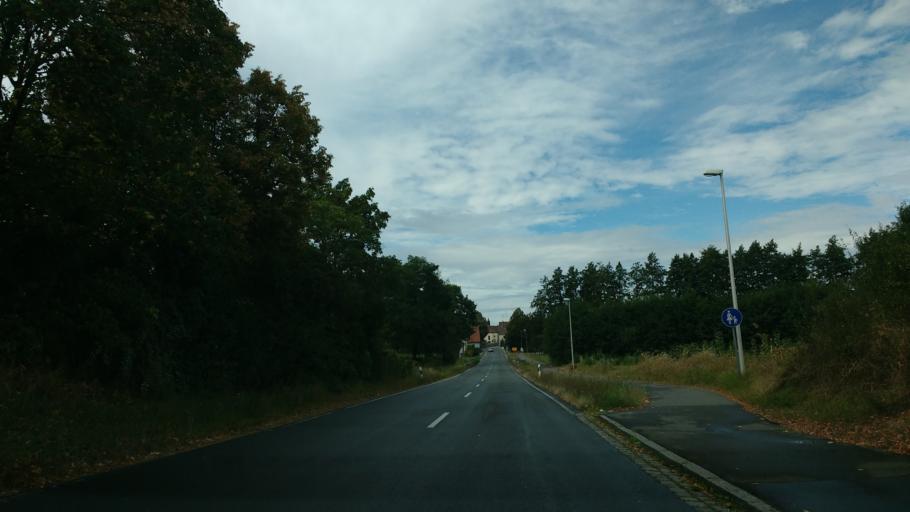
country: DE
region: Bavaria
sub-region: Upper Franconia
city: Schlusselfeld
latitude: 49.7584
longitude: 10.6134
